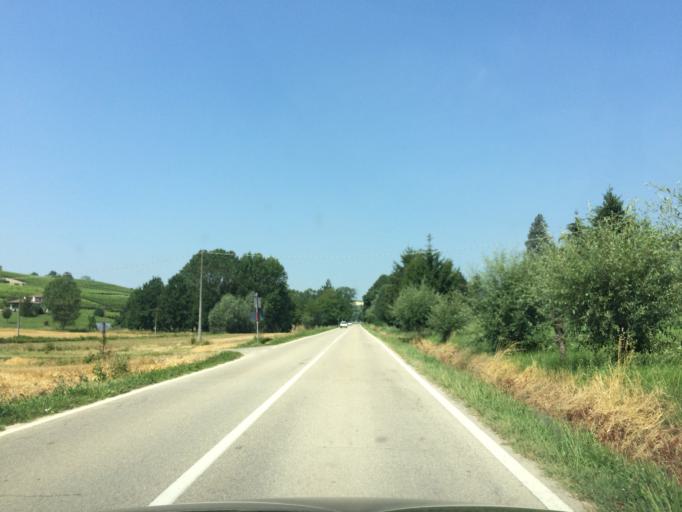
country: IT
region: Piedmont
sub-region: Provincia di Asti
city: Castelnuovo Calcea
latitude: 44.7774
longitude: 8.2742
